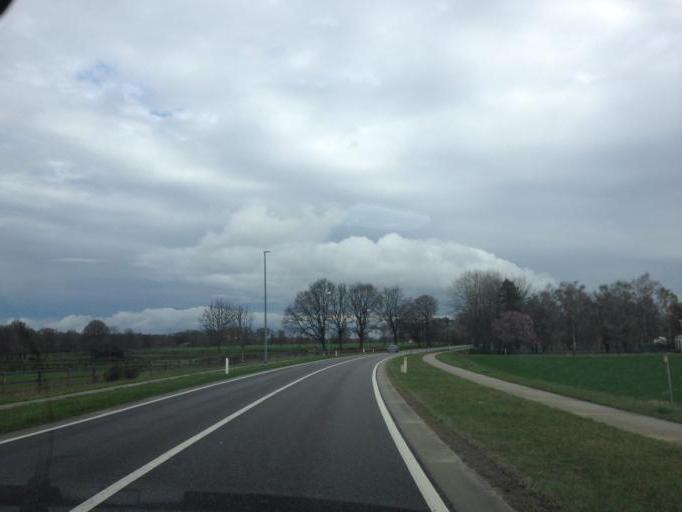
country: BE
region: Flanders
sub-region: Provincie Limburg
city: Bree
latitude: 51.1194
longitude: 5.5535
